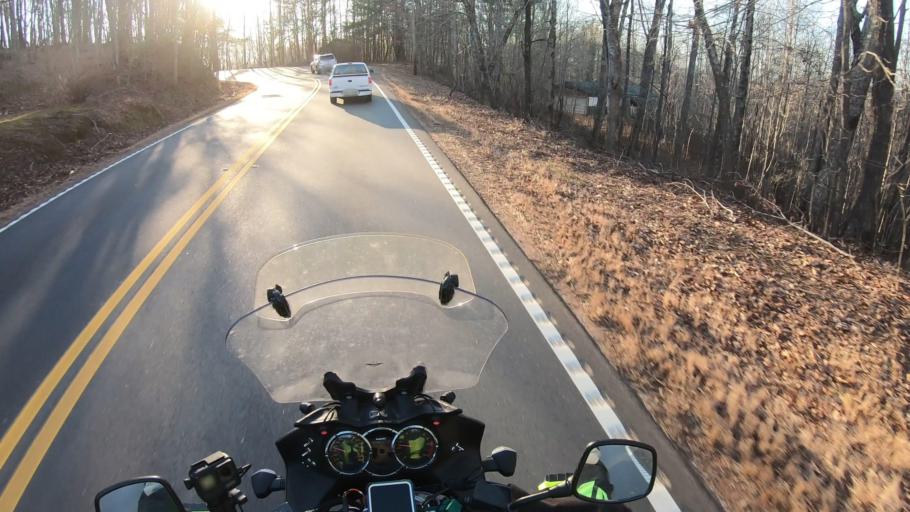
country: US
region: Georgia
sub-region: Lumpkin County
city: Dahlonega
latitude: 34.5823
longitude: -83.9705
